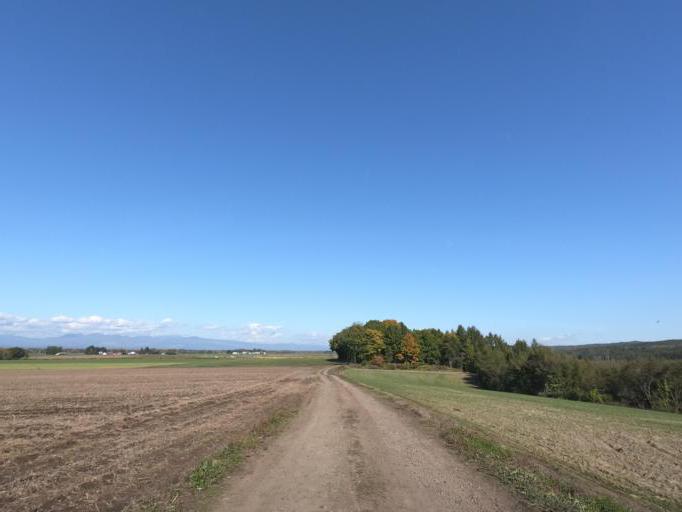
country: JP
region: Hokkaido
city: Otofuke
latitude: 43.0122
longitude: 143.2695
